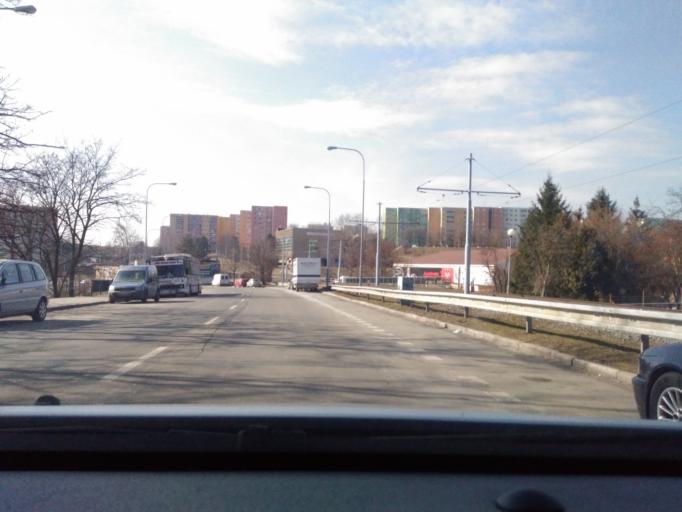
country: CZ
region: South Moravian
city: Moravany
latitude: 49.1702
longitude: 16.5782
